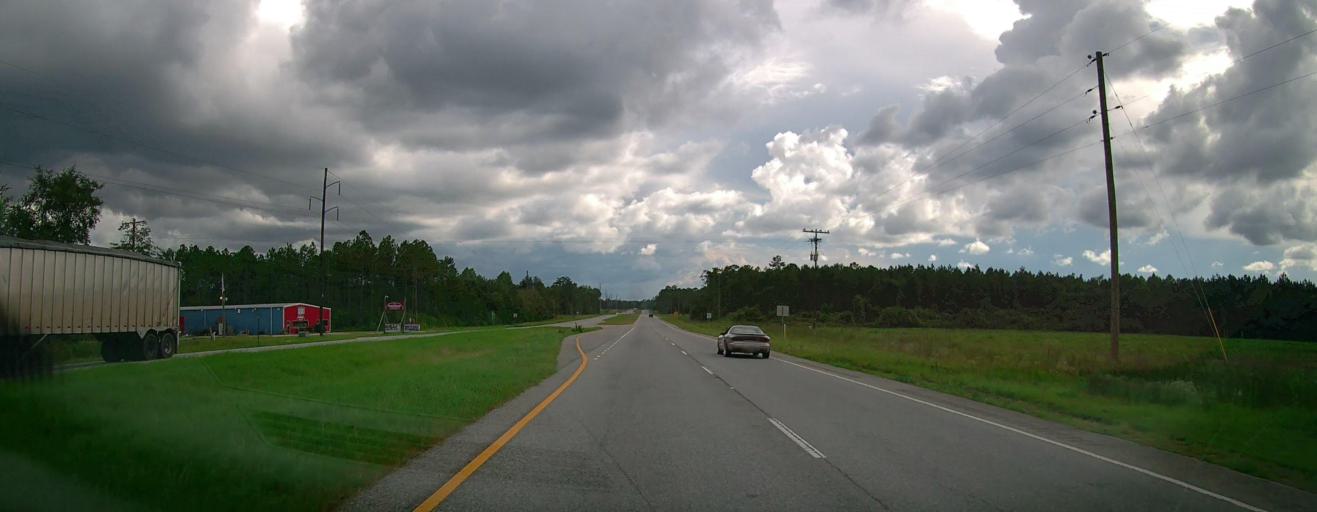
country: US
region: Georgia
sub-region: Pierce County
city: Blackshear
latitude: 31.4254
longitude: -82.0961
